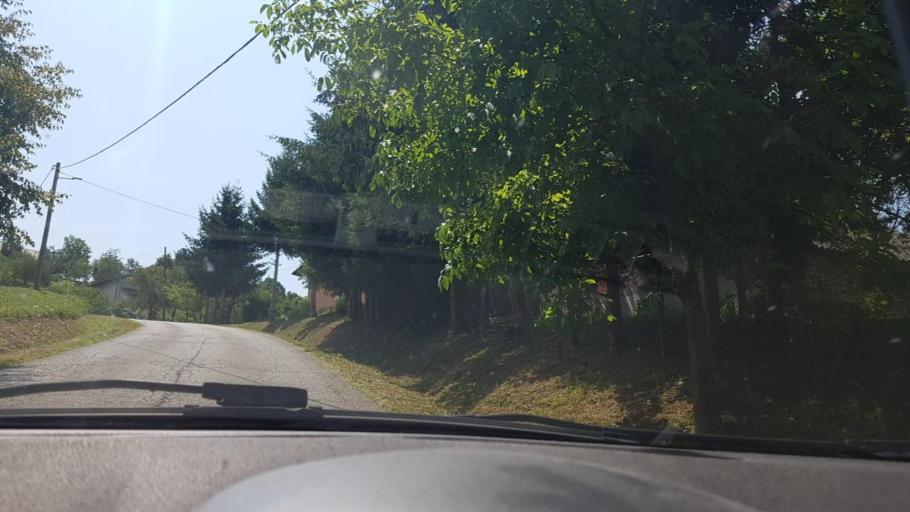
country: SI
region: Rogaska Slatina
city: Rogaska Slatina
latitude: 46.2116
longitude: 15.6466
